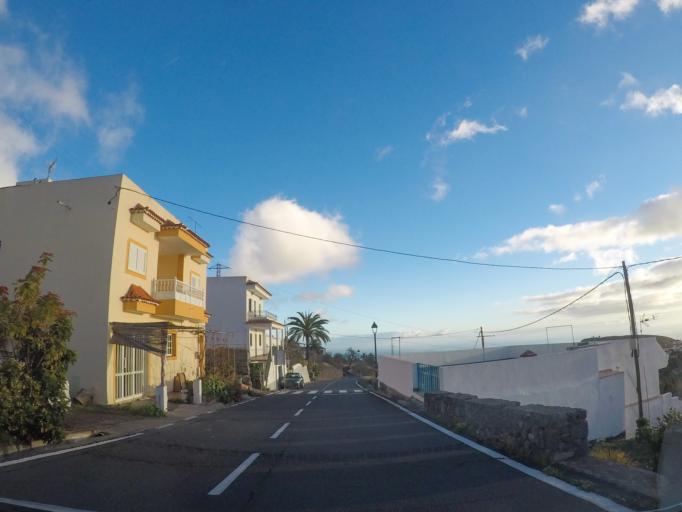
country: ES
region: Canary Islands
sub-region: Provincia de Santa Cruz de Tenerife
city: Alajero
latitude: 28.0642
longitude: -17.2373
